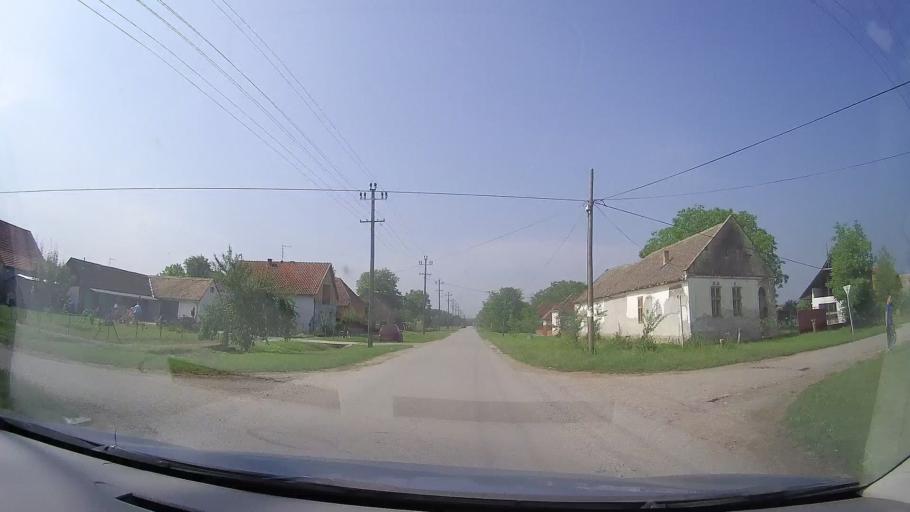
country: RS
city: Jasa Tomic
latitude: 45.4425
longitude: 20.8521
